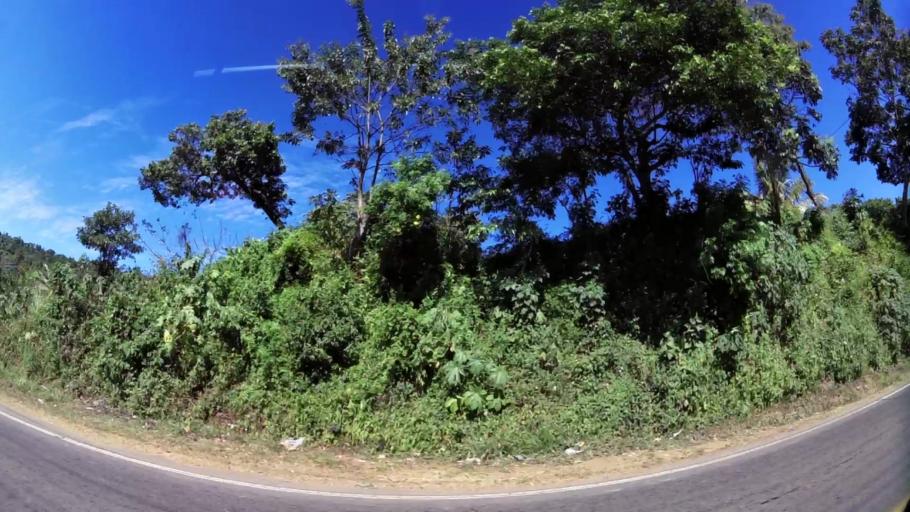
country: SV
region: Sonsonate
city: Juayua
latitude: 13.8370
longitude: -89.7640
